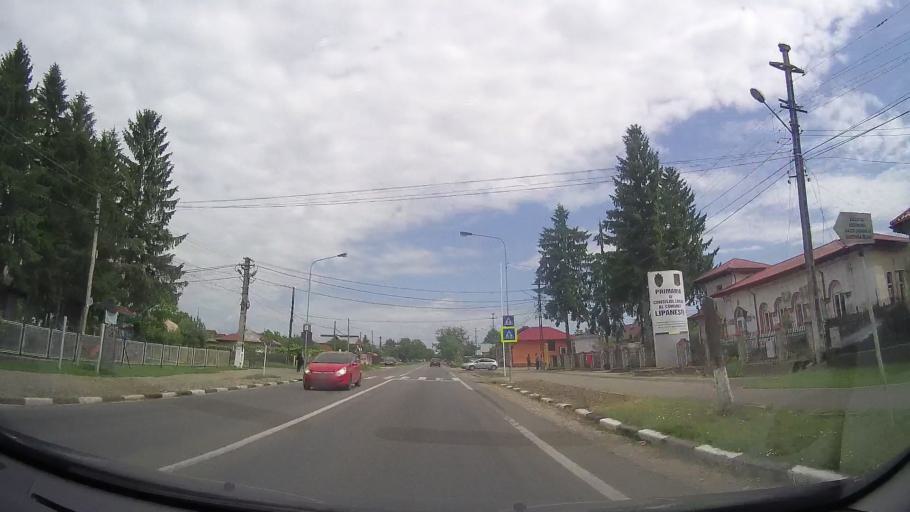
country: RO
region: Prahova
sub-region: Comuna Lipanesti
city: Lipanesti
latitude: 45.0555
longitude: 26.0202
